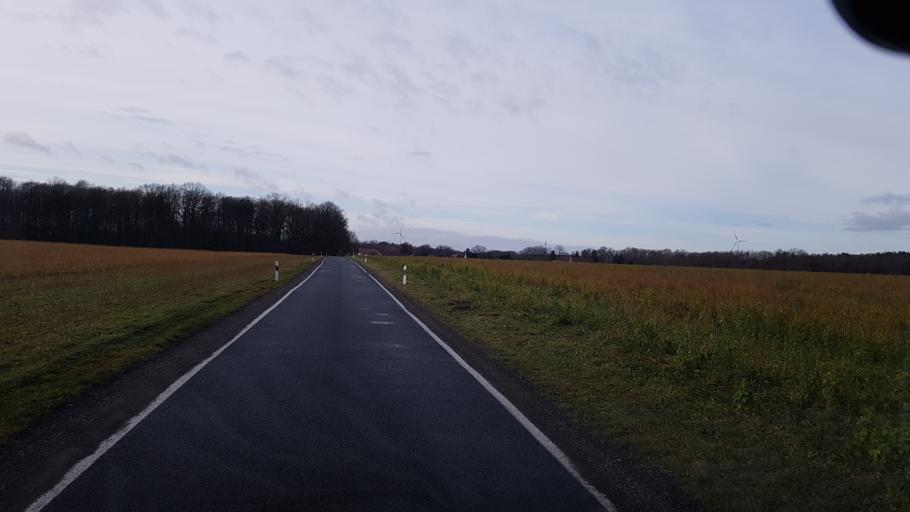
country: DE
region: Brandenburg
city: Bronkow
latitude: 51.6689
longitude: 13.9249
